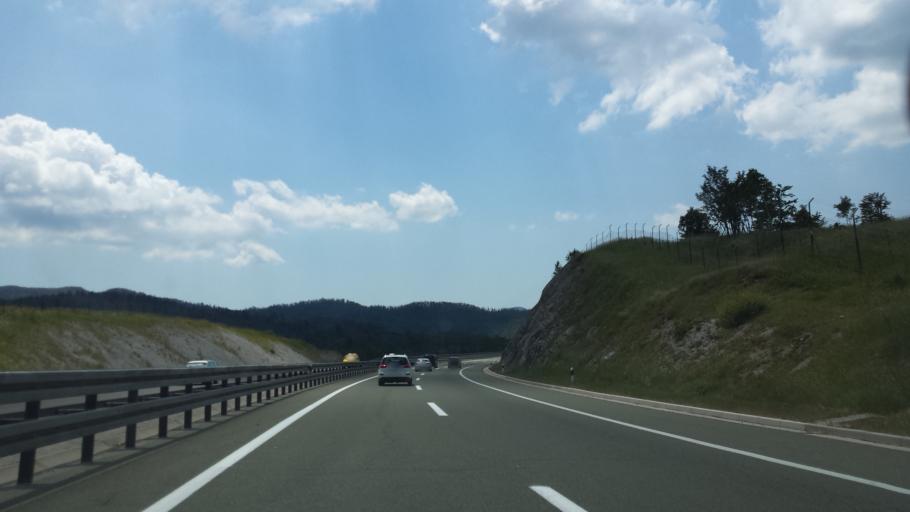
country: HR
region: Primorsko-Goranska
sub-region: Grad Delnice
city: Delnice
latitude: 45.3293
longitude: 14.7391
